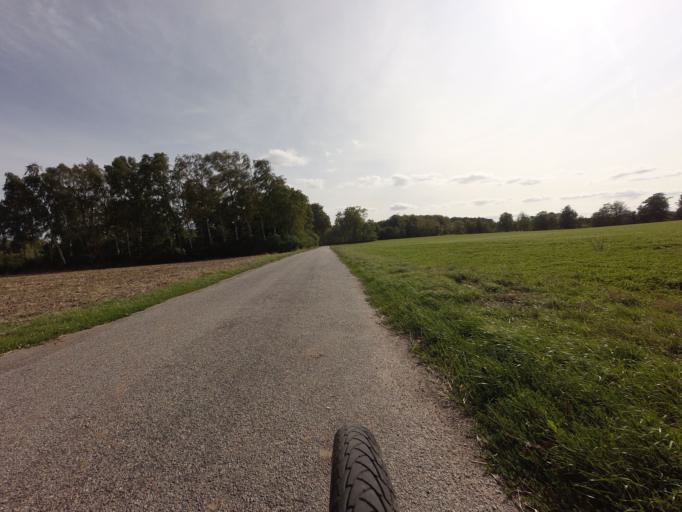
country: DK
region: Zealand
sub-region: Faxe Kommune
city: Fakse
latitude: 55.2077
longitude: 12.1229
